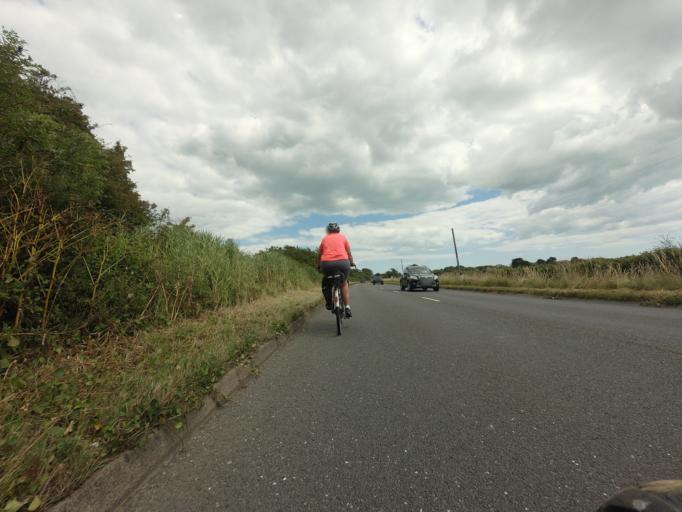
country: GB
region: England
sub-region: East Sussex
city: Pevensey
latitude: 50.8168
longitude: 0.3465
